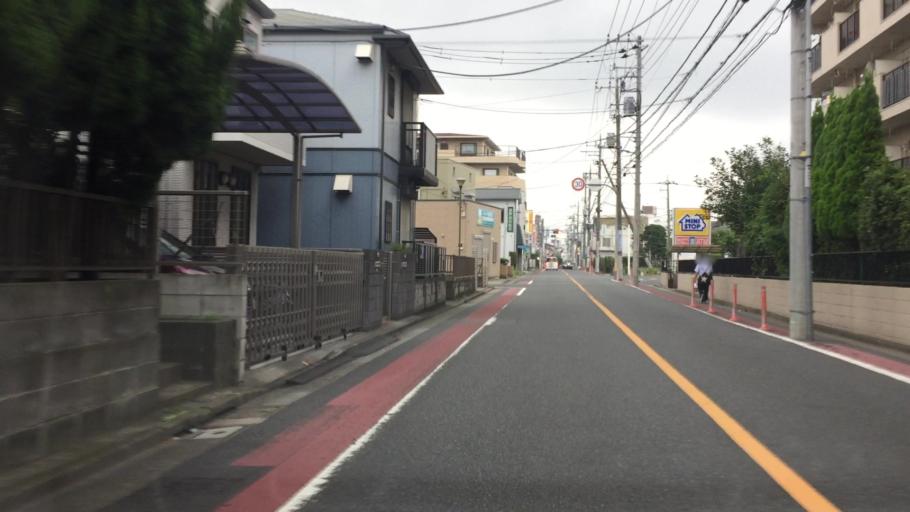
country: JP
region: Chiba
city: Matsudo
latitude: 35.7470
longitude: 139.8382
